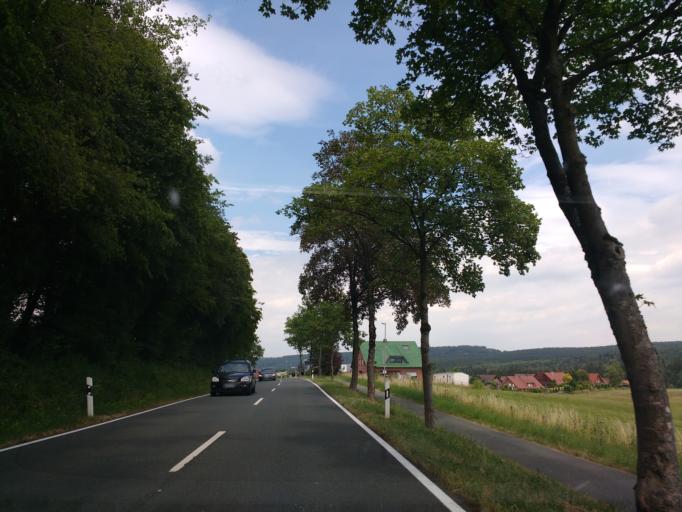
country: DE
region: North Rhine-Westphalia
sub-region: Regierungsbezirk Detmold
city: Altenbeken
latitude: 51.7484
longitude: 8.9464
